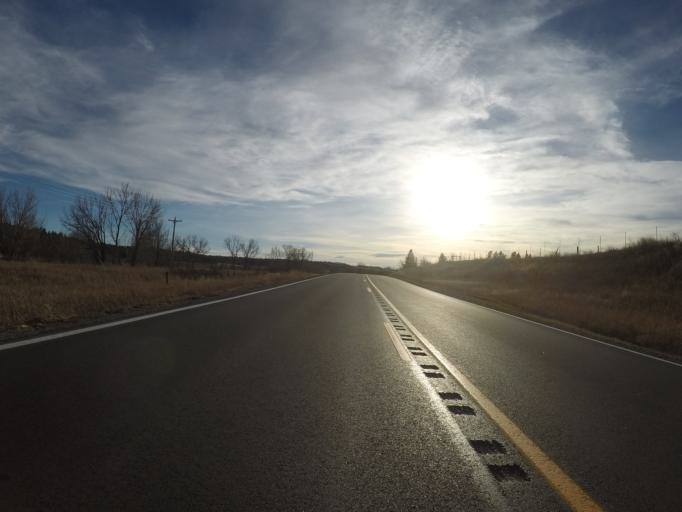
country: US
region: Montana
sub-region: Musselshell County
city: Roundup
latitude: 46.4065
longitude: -108.5961
